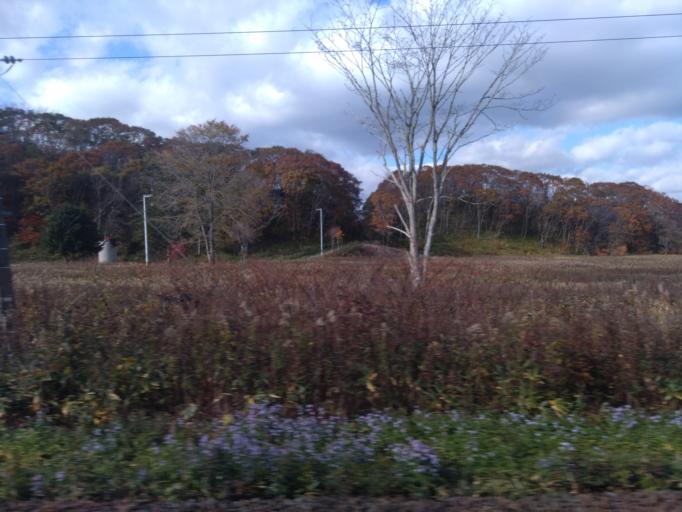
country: JP
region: Hokkaido
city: Shiraoi
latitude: 42.5670
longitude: 141.3823
